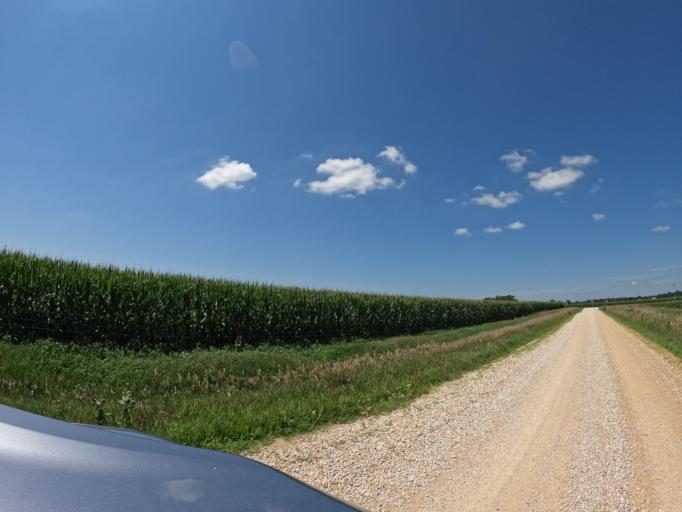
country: US
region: Iowa
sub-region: Clinton County
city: De Witt
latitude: 41.7793
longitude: -90.4113
